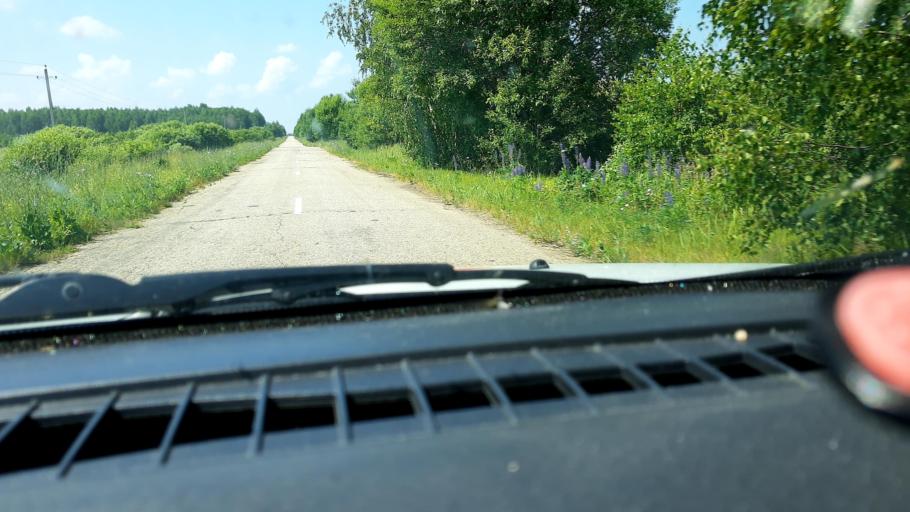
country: RU
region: Nizjnij Novgorod
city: Sharanga
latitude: 57.0643
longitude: 46.6531
